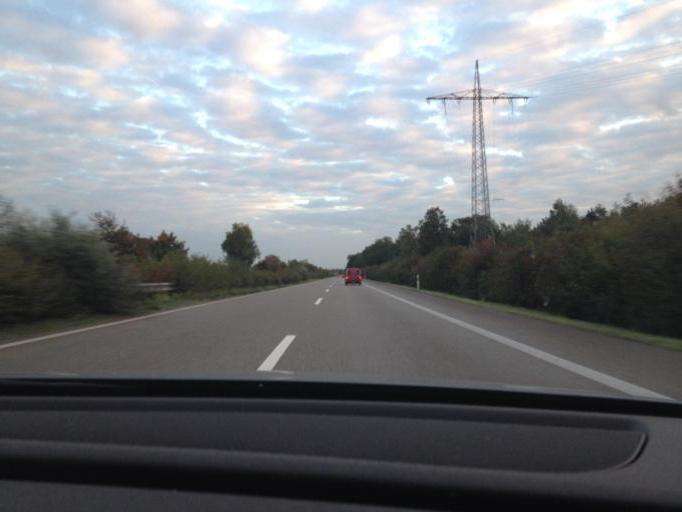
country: DE
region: Rheinland-Pfalz
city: Waldsee
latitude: 49.3780
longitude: 8.4201
